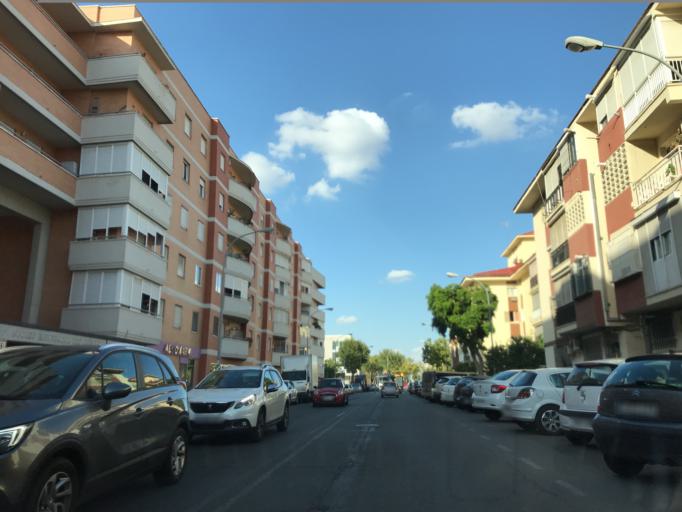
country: ES
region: Andalusia
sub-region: Provincia de Sevilla
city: Sevilla
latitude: 37.4075
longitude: -5.9285
